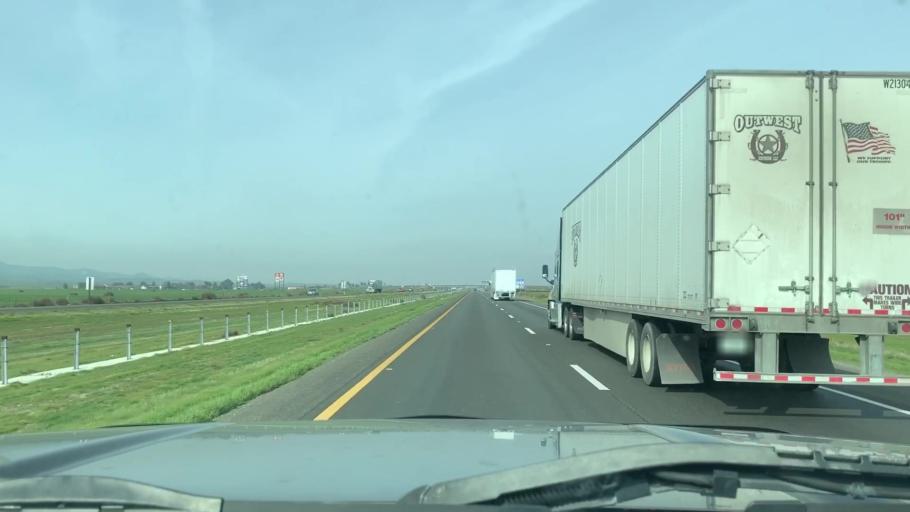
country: US
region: California
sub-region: Fresno County
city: Huron
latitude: 36.2459
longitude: -120.2385
